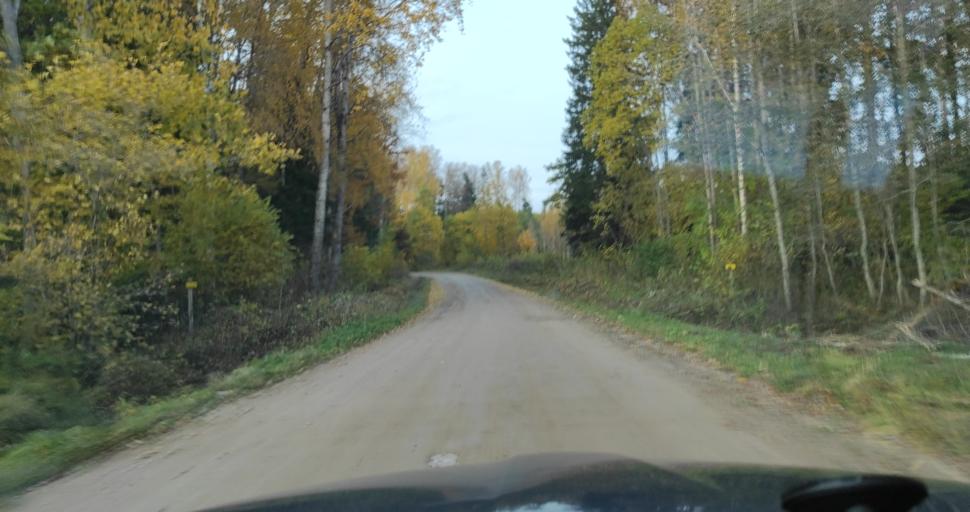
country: LV
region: Vainode
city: Vainode
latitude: 56.6298
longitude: 21.8167
